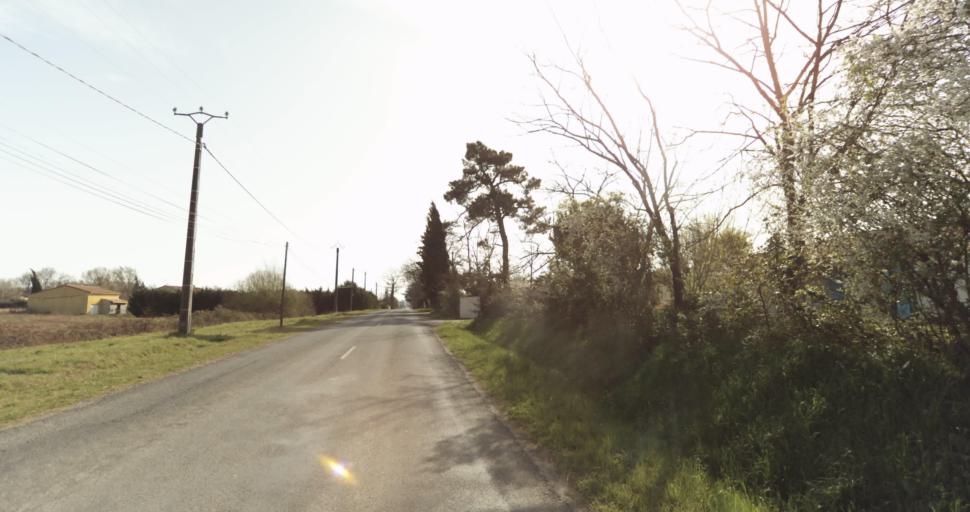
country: FR
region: Midi-Pyrenees
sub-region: Departement du Tarn
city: Saint-Sulpice-la-Pointe
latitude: 43.7690
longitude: 1.7093
